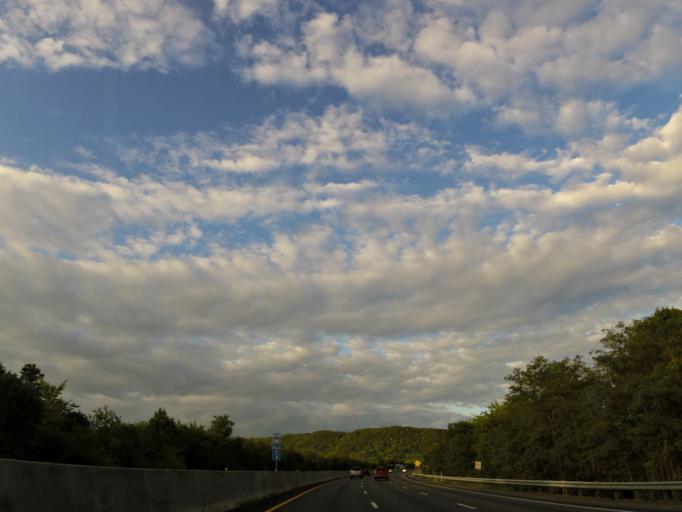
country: US
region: Tennessee
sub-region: Hamilton County
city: Collegedale
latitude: 35.1241
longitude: -85.0401
